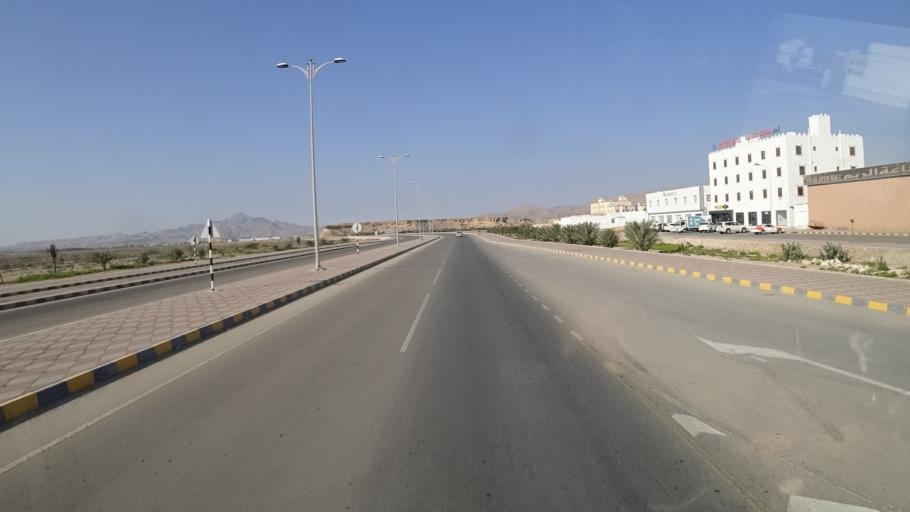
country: OM
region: Ash Sharqiyah
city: Sur
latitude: 22.6003
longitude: 59.4814
